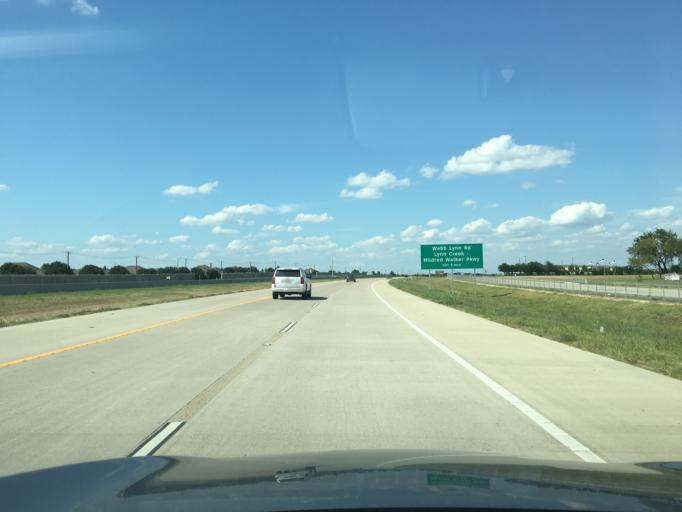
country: US
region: Texas
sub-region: Tarrant County
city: Mansfield
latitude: 32.6143
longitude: -97.0763
